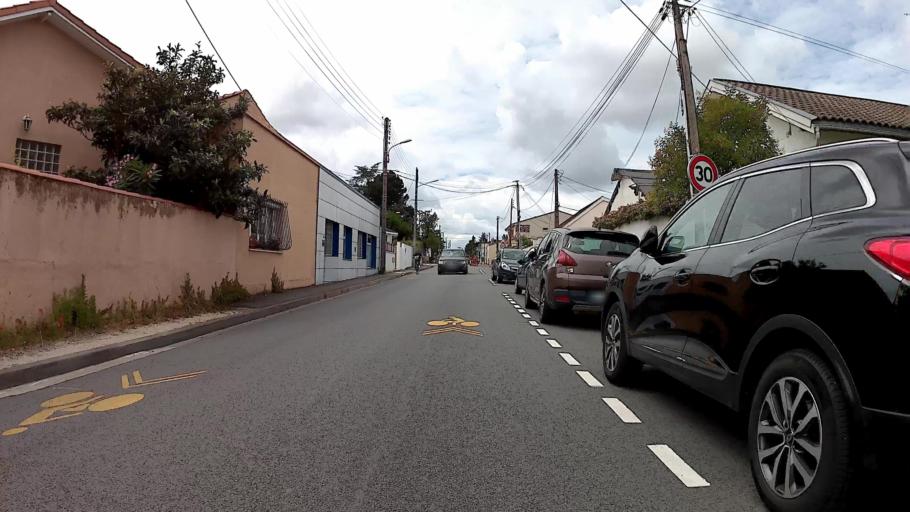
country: FR
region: Aquitaine
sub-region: Departement de la Gironde
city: Merignac
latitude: 44.8162
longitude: -0.6191
